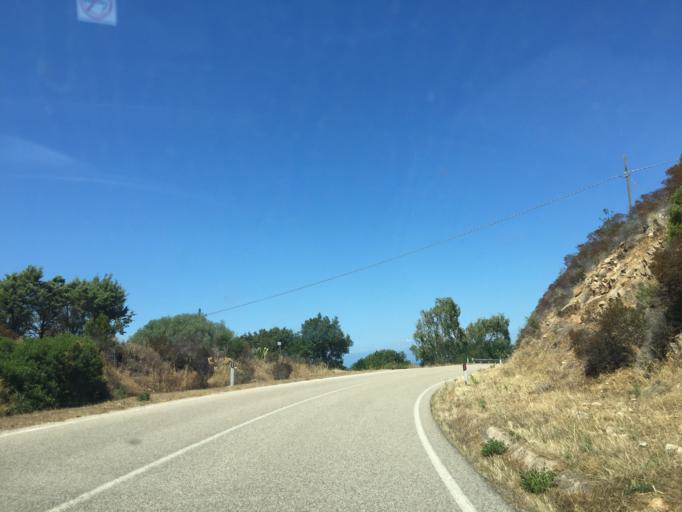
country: IT
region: Sardinia
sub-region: Provincia di Olbia-Tempio
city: Aglientu
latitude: 41.1000
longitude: 9.0830
